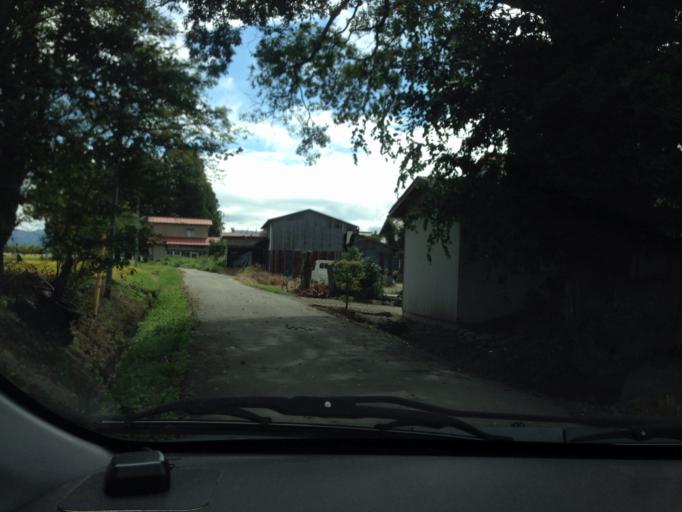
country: JP
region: Fukushima
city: Kitakata
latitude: 37.4932
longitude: 139.8669
